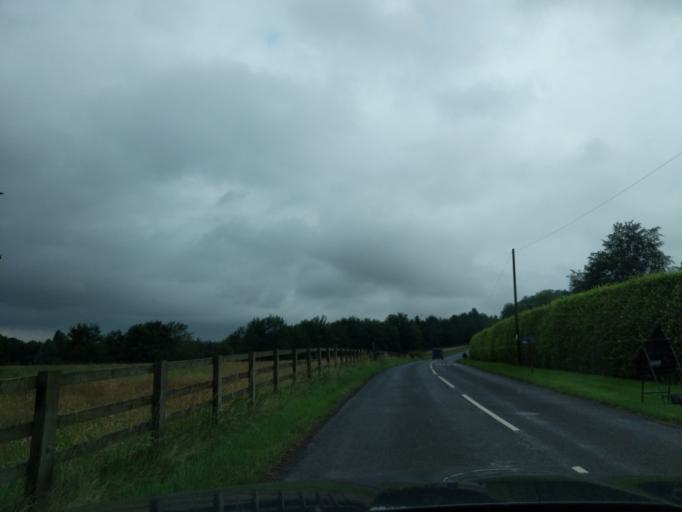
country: GB
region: England
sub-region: Northumberland
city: Ford
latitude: 55.6487
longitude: -2.1163
